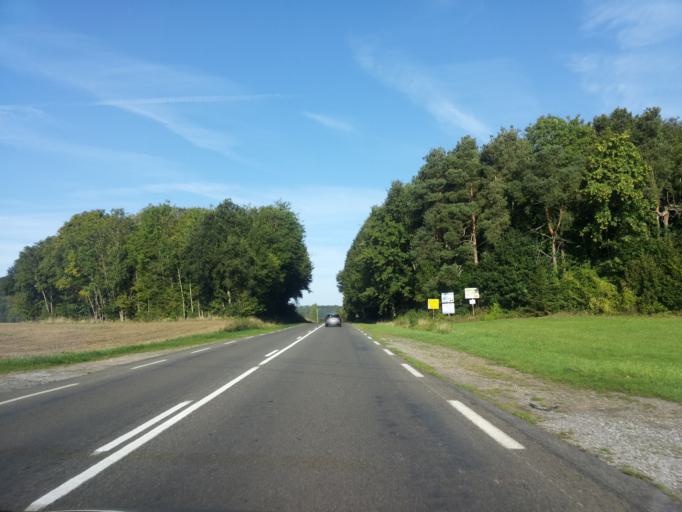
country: FR
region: Picardie
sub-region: Departement de l'Aisne
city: Crepy
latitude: 49.5952
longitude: 3.5318
